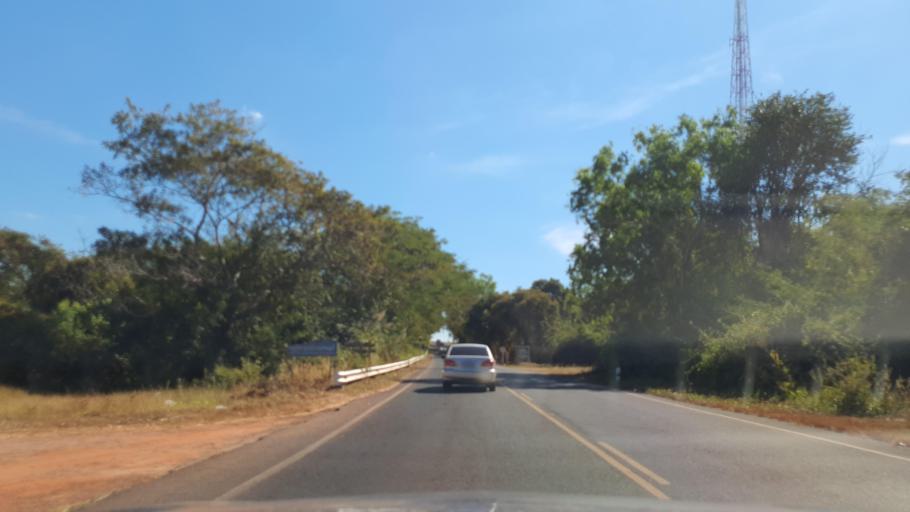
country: TH
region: Kalasin
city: Khao Wong
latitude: 16.7691
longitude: 104.1543
